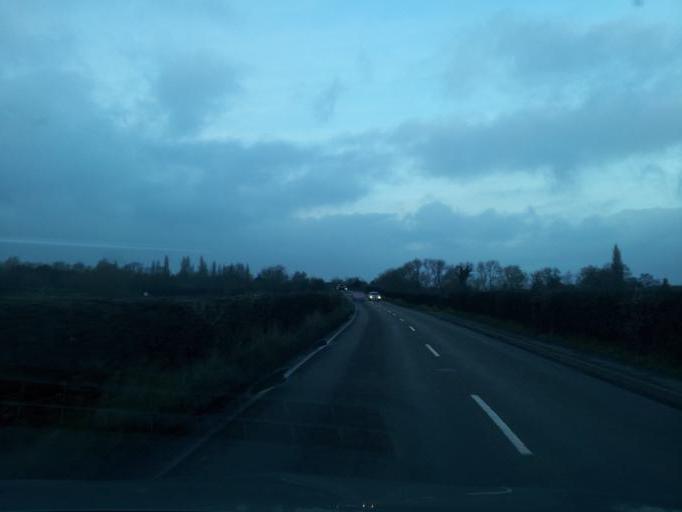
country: GB
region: England
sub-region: Derbyshire
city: Repton
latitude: 52.8465
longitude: -1.5600
